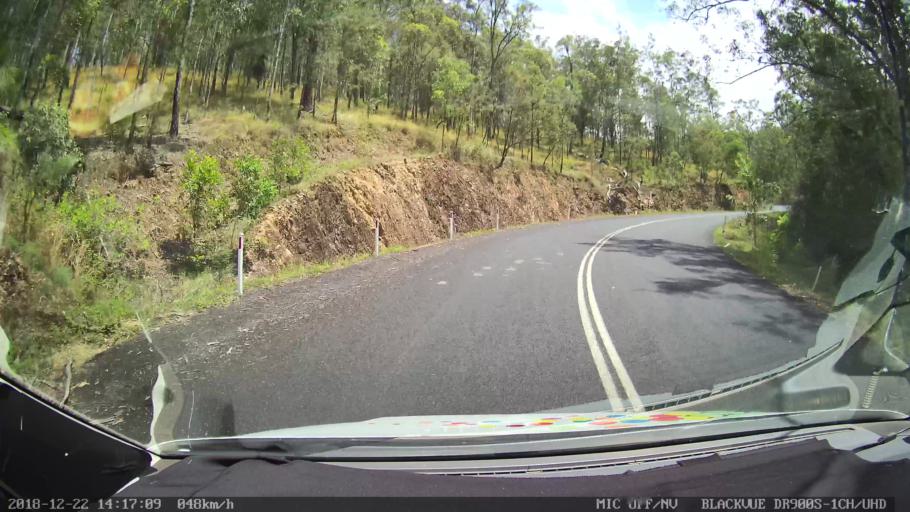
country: AU
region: New South Wales
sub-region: Clarence Valley
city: Coutts Crossing
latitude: -30.0069
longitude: 152.6686
